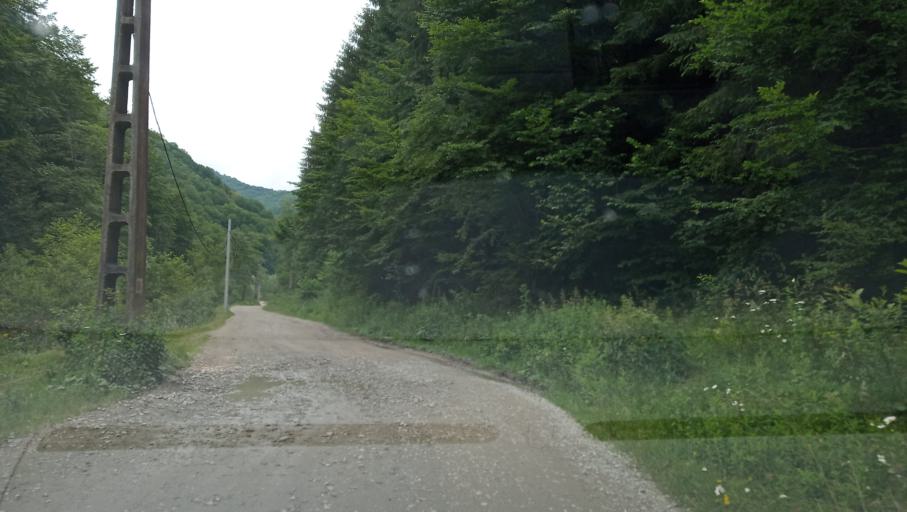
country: RO
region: Hunedoara
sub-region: Oras Petrila
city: Petrila
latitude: 45.4768
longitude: 23.4160
